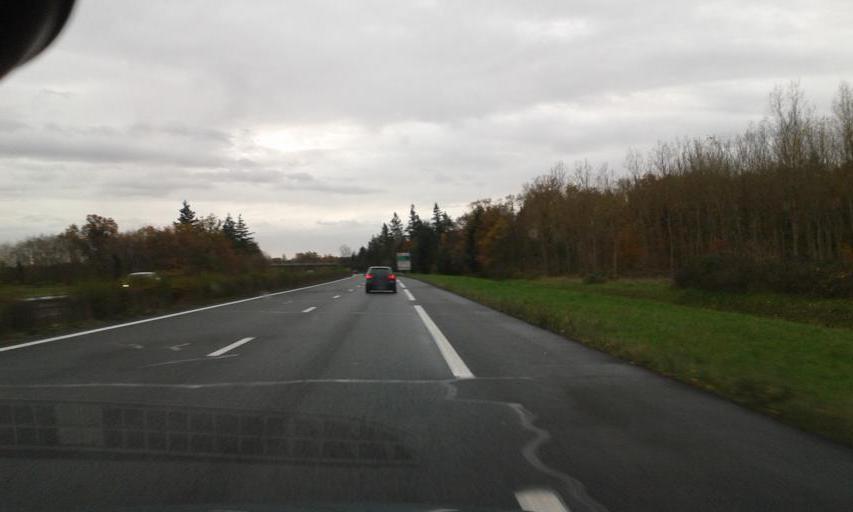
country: FR
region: Centre
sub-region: Departement du Loiret
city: Chateauneuf-sur-Loire
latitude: 47.8875
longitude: 2.2203
